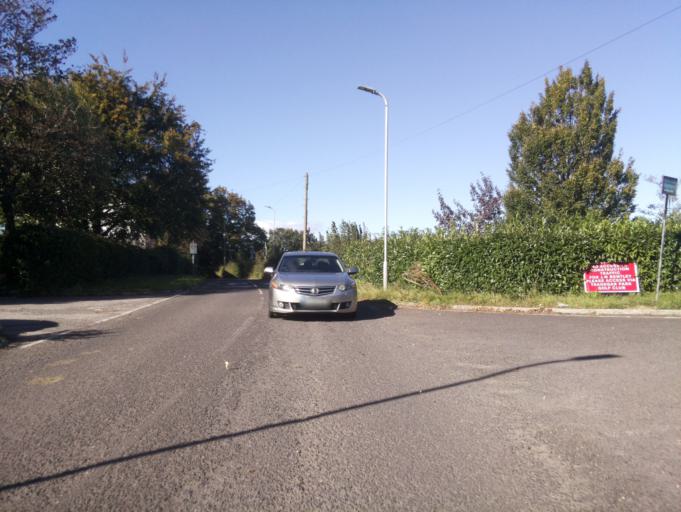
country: GB
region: Wales
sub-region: Newport
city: Newport
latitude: 51.5922
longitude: -3.0424
